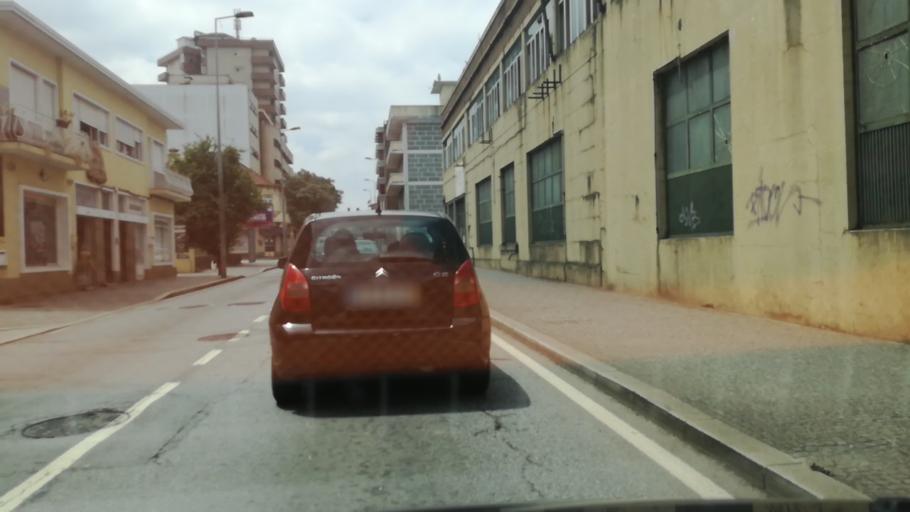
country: PT
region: Porto
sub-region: Trofa
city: Bougado
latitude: 41.3391
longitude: -8.5589
